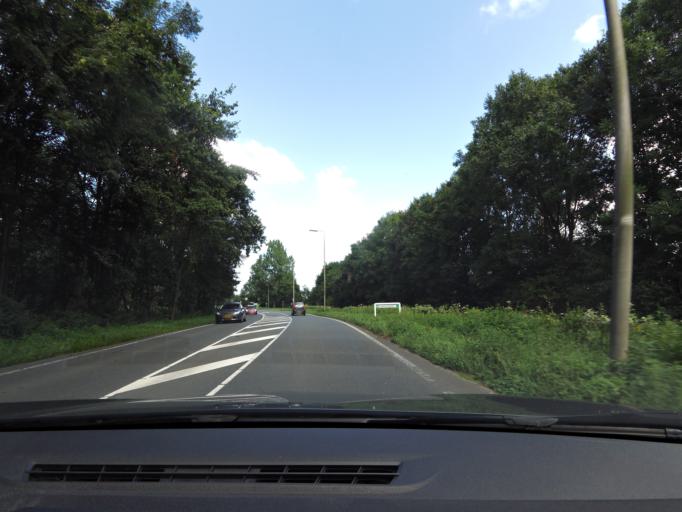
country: NL
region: South Holland
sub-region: Gemeente Alphen aan den Rijn
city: Alphen aan den Rijn
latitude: 52.1439
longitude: 4.7062
